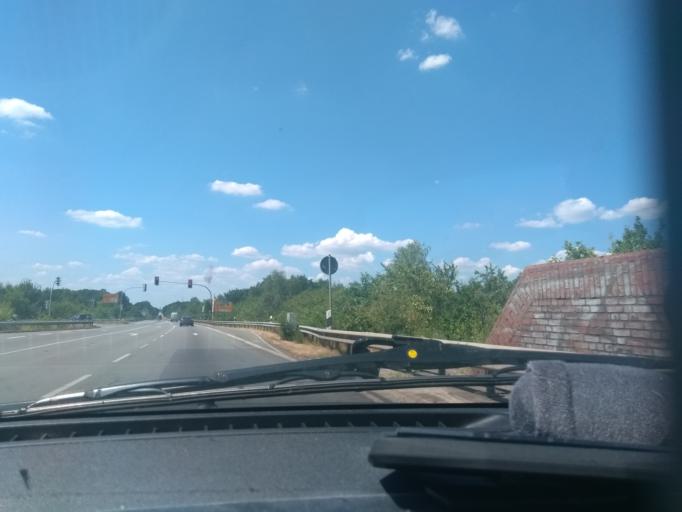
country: DE
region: Lower Saxony
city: Meppen
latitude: 52.7138
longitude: 7.2952
